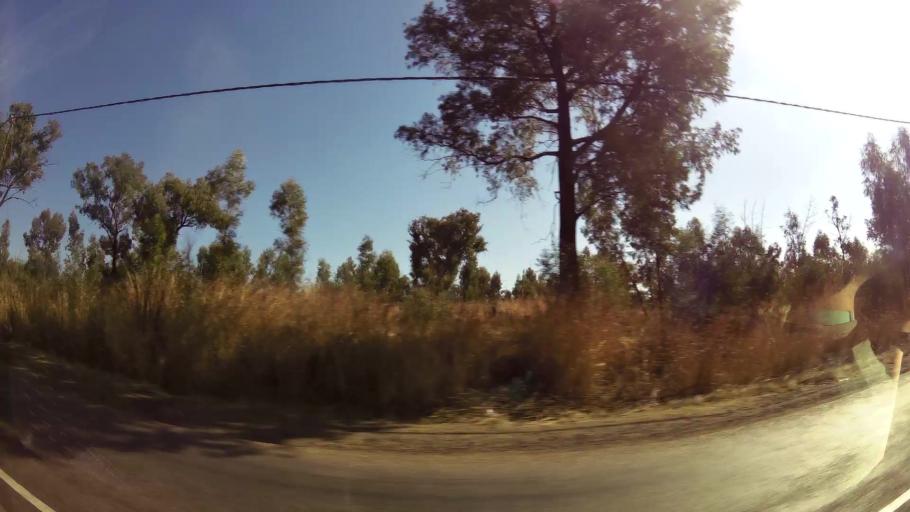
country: ZA
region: Mpumalanga
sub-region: Nkangala District Municipality
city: Witbank
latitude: -25.8424
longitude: 29.2387
